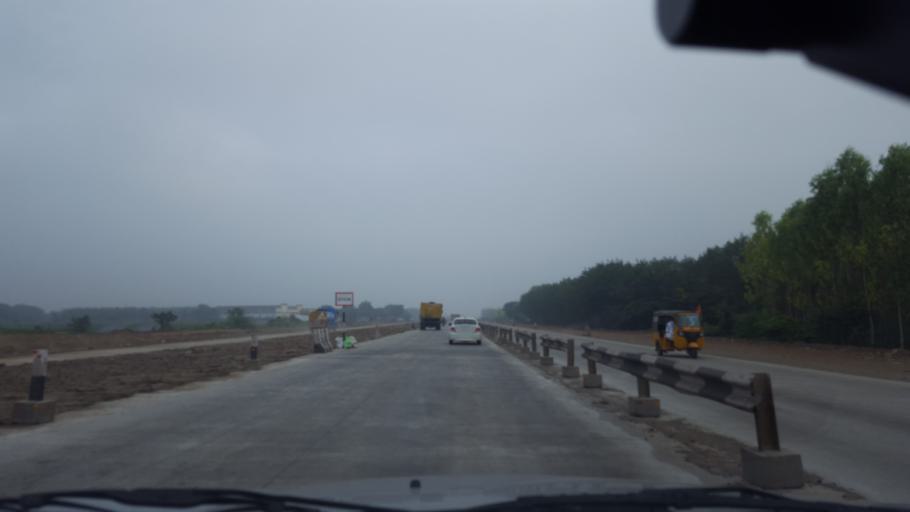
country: IN
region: Andhra Pradesh
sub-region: Prakasam
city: Addanki
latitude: 15.7901
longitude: 80.0379
